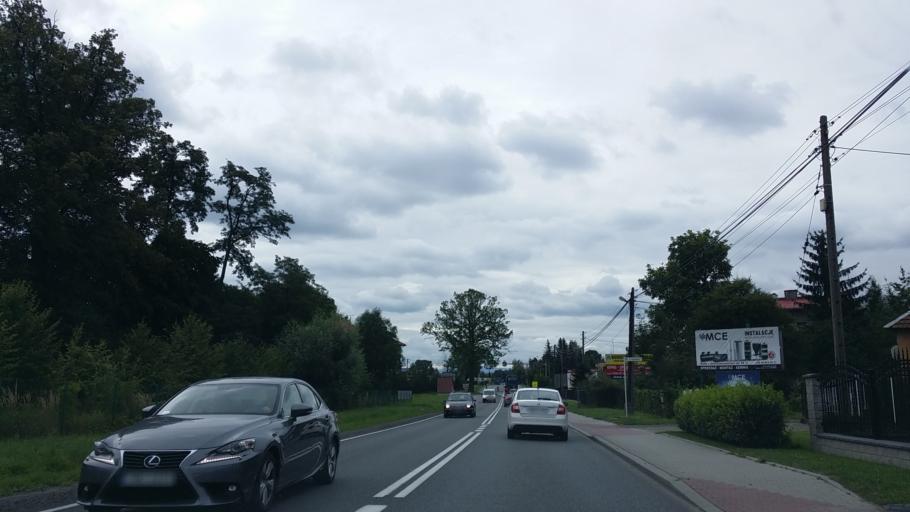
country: PL
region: Lesser Poland Voivodeship
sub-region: Powiat wadowicki
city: Tomice
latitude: 49.9024
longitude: 19.4843
